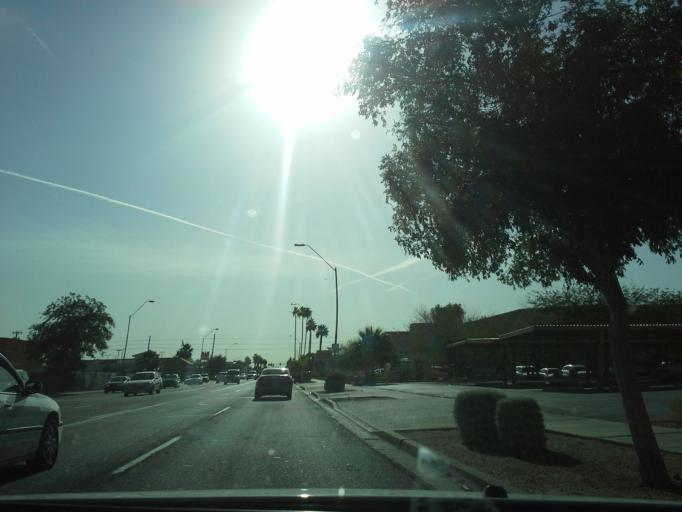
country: US
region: Arizona
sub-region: Maricopa County
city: Phoenix
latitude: 33.4653
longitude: -112.0623
